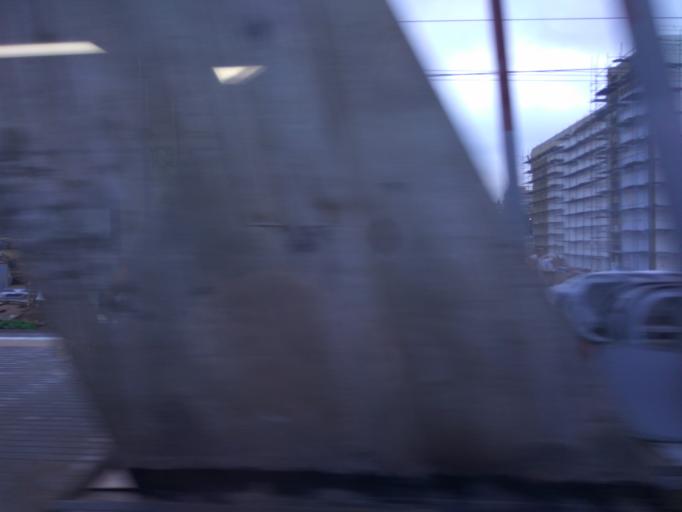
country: RU
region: Moscow
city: Sokol
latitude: 55.7890
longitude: 37.5044
